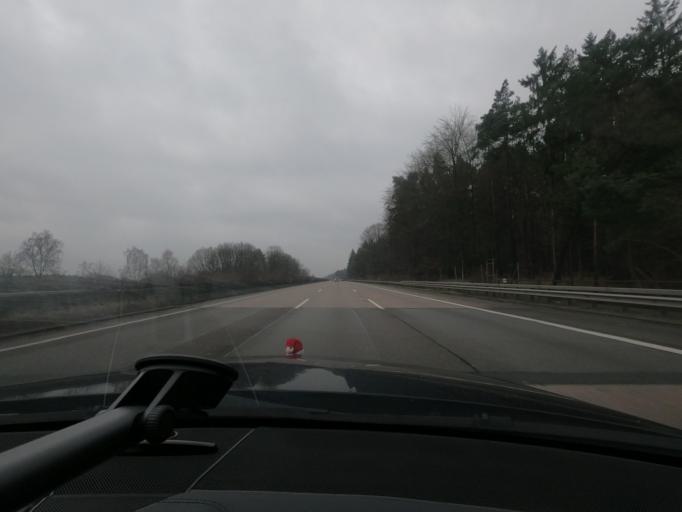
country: DE
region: Lower Saxony
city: Toppenstedt
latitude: 53.2833
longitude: 10.0795
